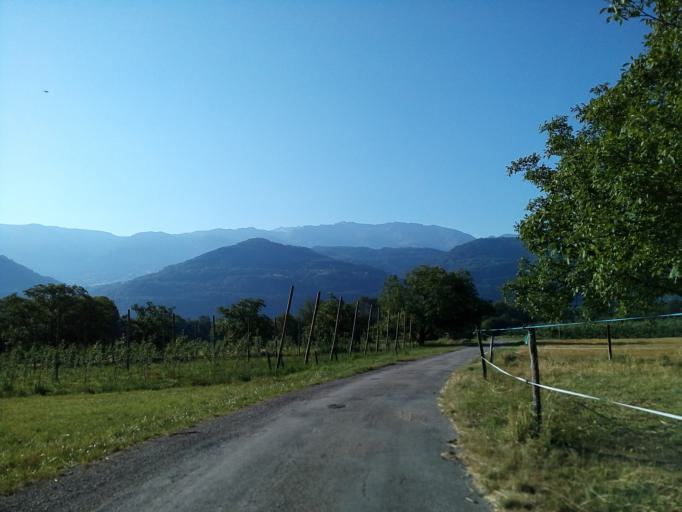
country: FR
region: Rhone-Alpes
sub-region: Departement de l'Isere
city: La Terrasse
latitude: 45.3146
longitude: 5.9289
